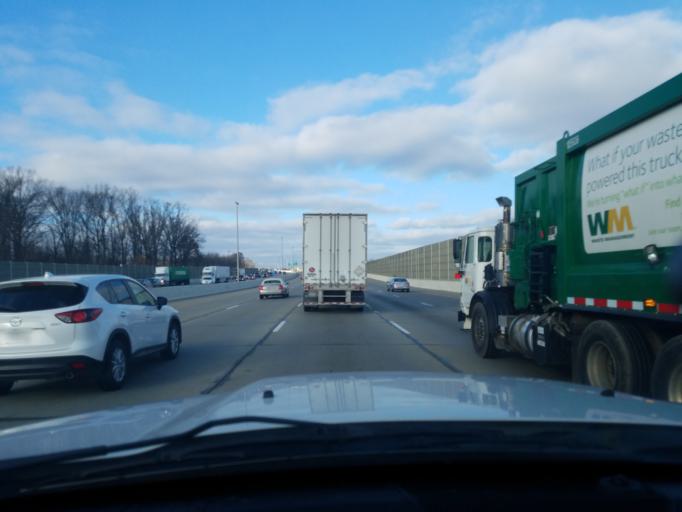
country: US
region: Indiana
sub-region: Marion County
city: Speedway
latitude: 39.7547
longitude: -86.2645
